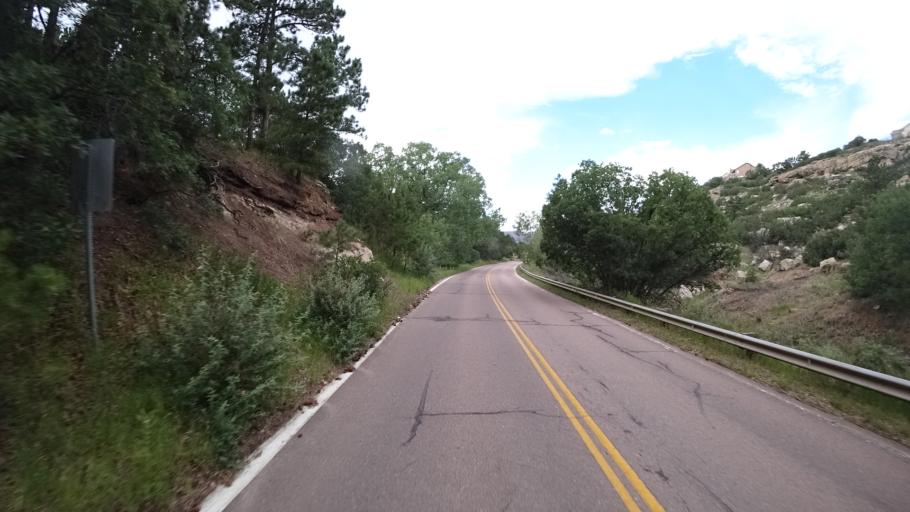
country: US
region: Colorado
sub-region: El Paso County
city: Colorado Springs
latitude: 38.9070
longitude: -104.8338
